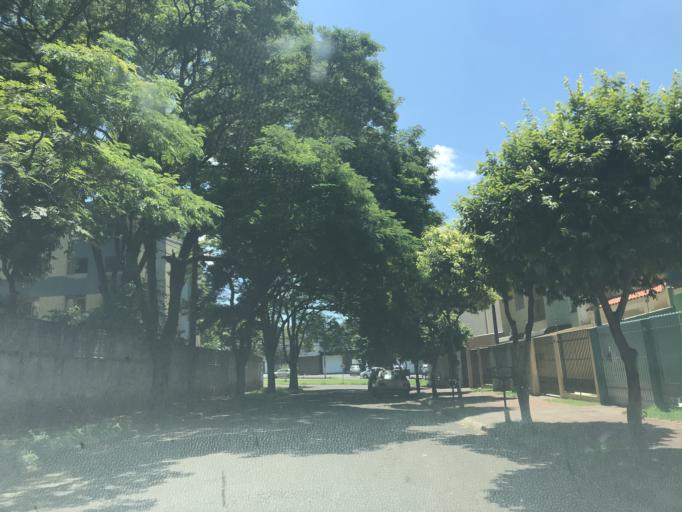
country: BR
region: Parana
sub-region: Maringa
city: Maringa
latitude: -23.4493
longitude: -51.9332
